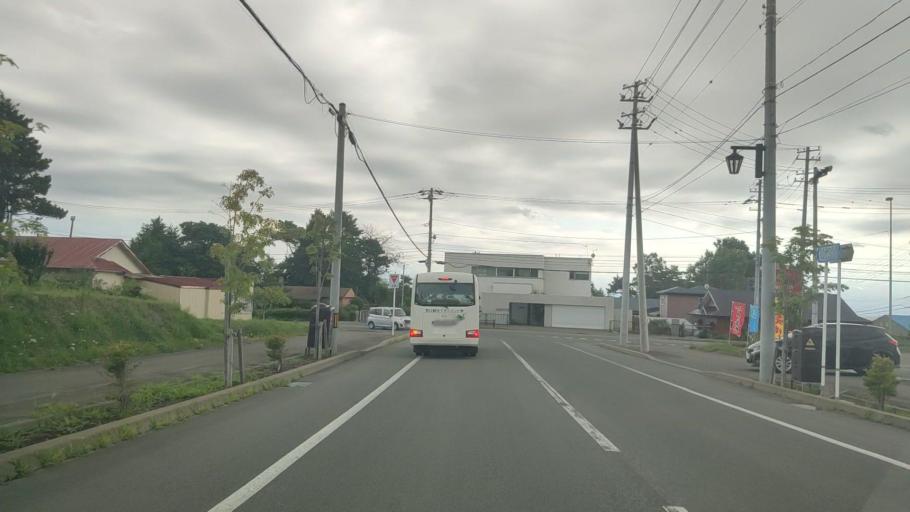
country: JP
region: Hokkaido
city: Date
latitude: 42.5510
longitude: 140.7696
